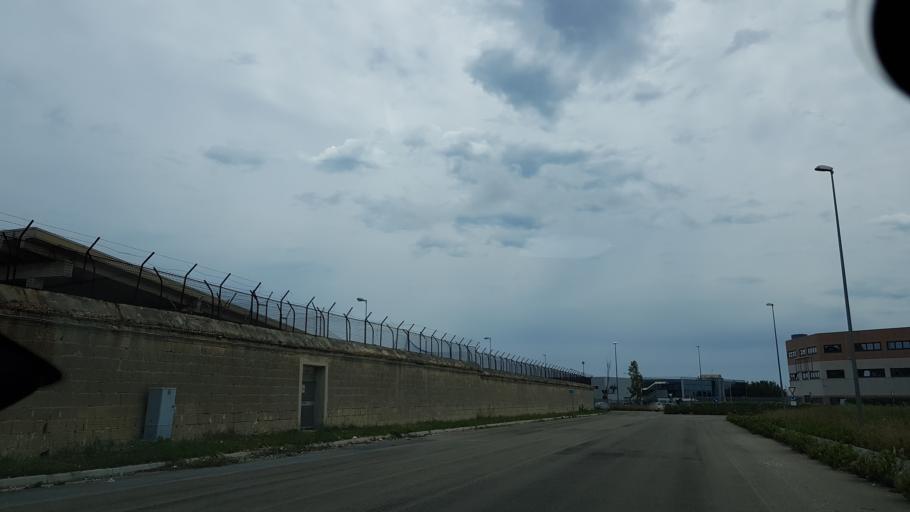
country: IT
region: Apulia
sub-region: Provincia di Brindisi
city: Brindisi
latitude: 40.6342
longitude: 17.9572
